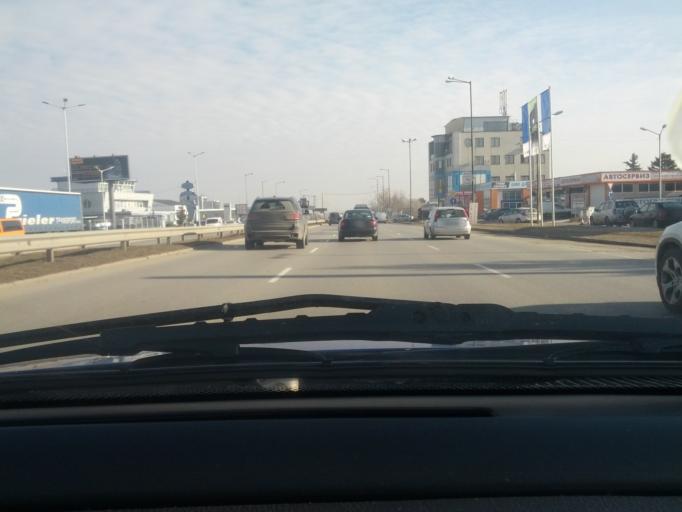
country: BG
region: Sofia-Capital
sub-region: Stolichna Obshtina
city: Sofia
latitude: 42.7091
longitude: 23.4278
